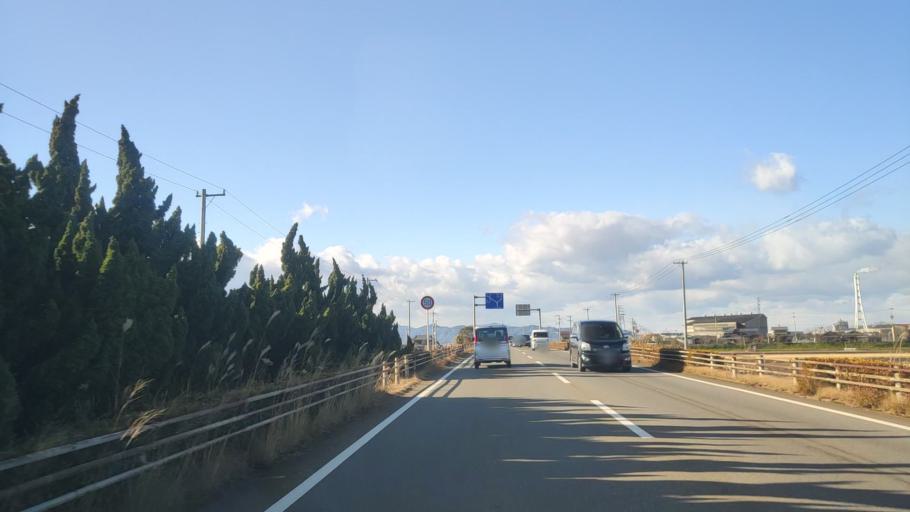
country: JP
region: Ehime
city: Saijo
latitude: 33.9175
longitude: 133.1275
